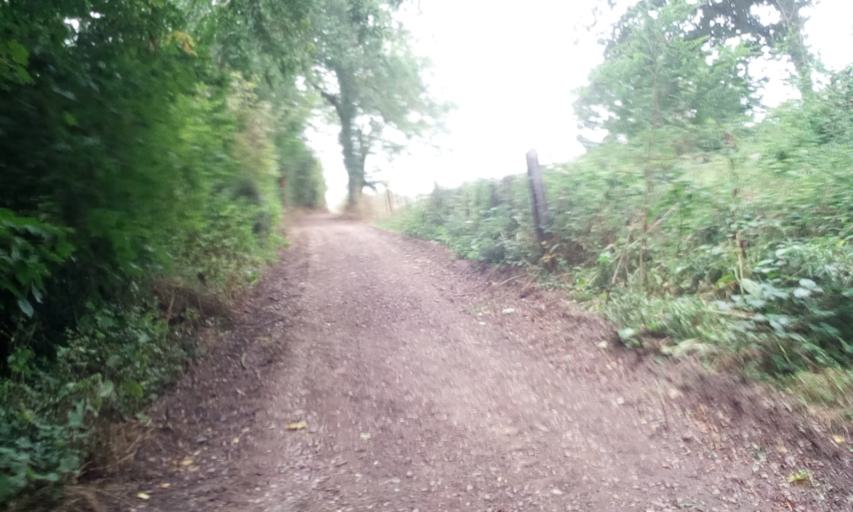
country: FR
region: Lower Normandy
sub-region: Departement du Calvados
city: Tourville-sur-Odon
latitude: 49.1342
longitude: -0.4953
